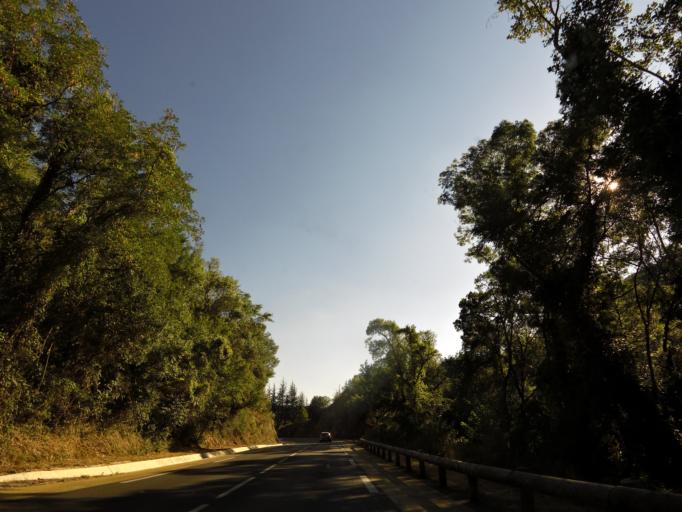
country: FR
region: Languedoc-Roussillon
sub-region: Departement de l'Herault
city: Ganges
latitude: 43.9594
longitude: 3.6876
